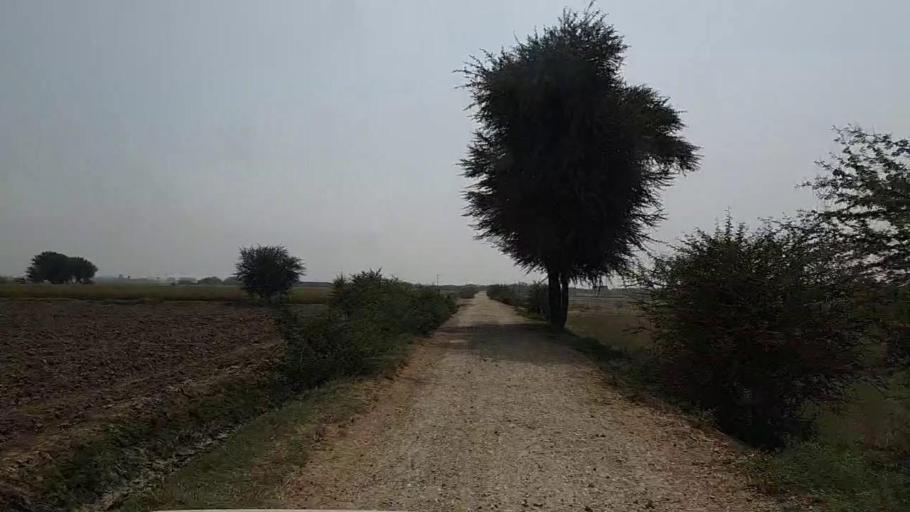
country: PK
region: Sindh
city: Naukot
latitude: 24.8162
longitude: 69.3595
